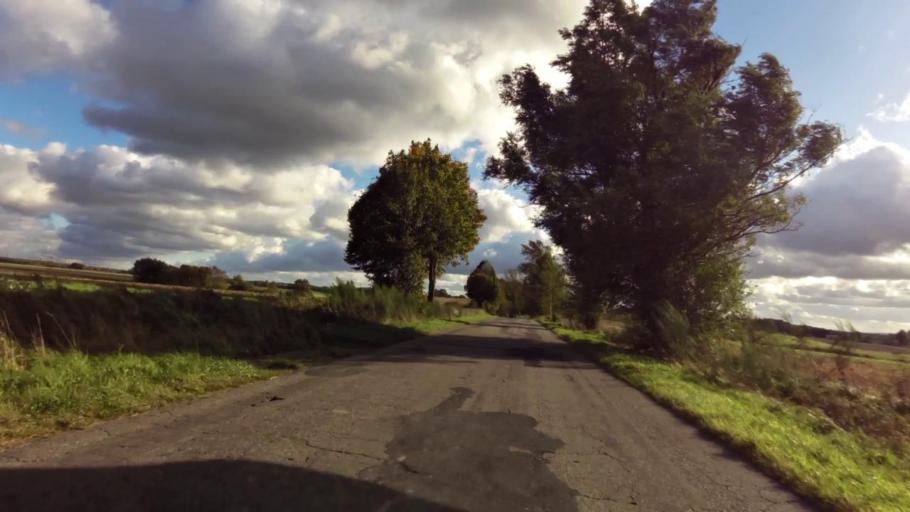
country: PL
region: West Pomeranian Voivodeship
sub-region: Powiat bialogardzki
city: Bialogard
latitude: 54.0262
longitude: 16.0599
